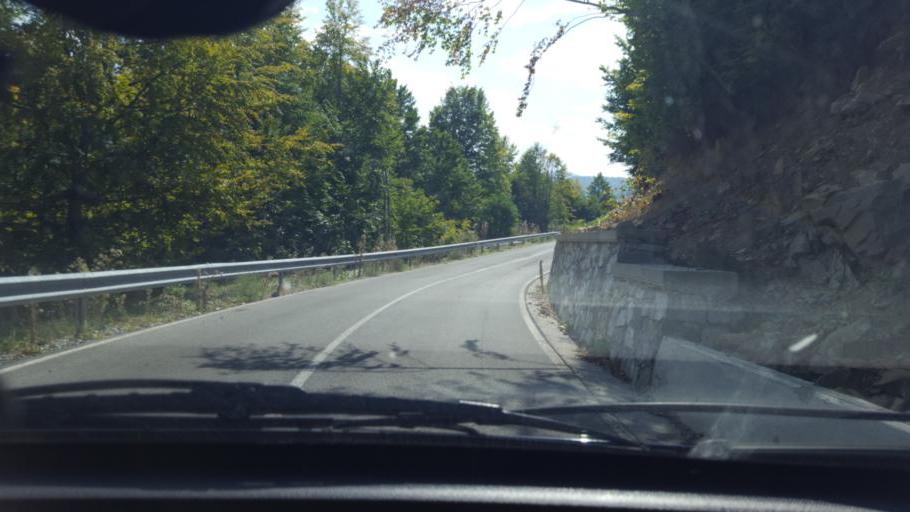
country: AL
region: Kukes
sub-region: Rrethi i Tropojes
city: Valbone
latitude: 42.5426
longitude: 19.7201
